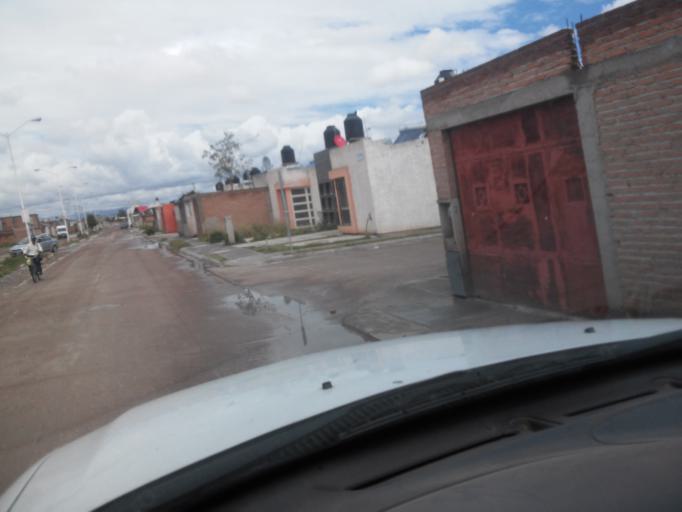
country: MX
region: Durango
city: Victoria de Durango
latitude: 24.0218
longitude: -104.6132
